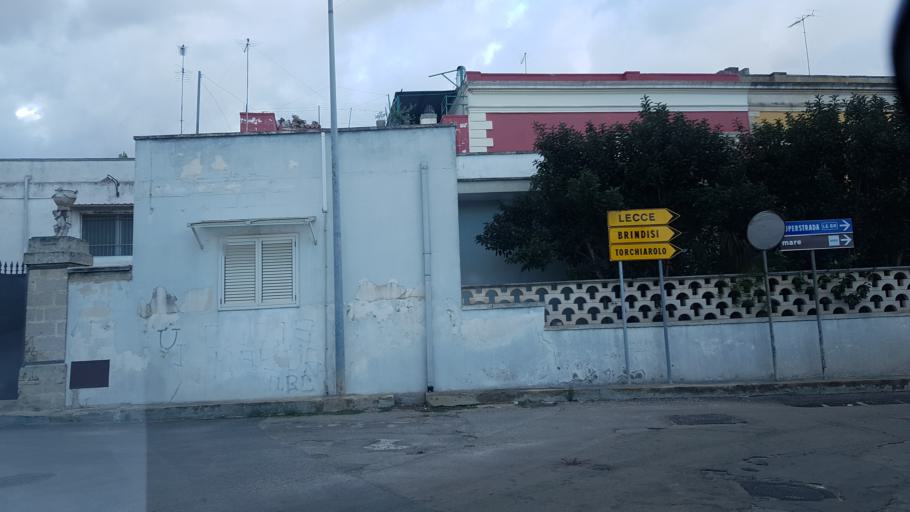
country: IT
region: Apulia
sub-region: Provincia di Brindisi
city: San Pietro Vernotico
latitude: 40.4925
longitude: 18.0005
